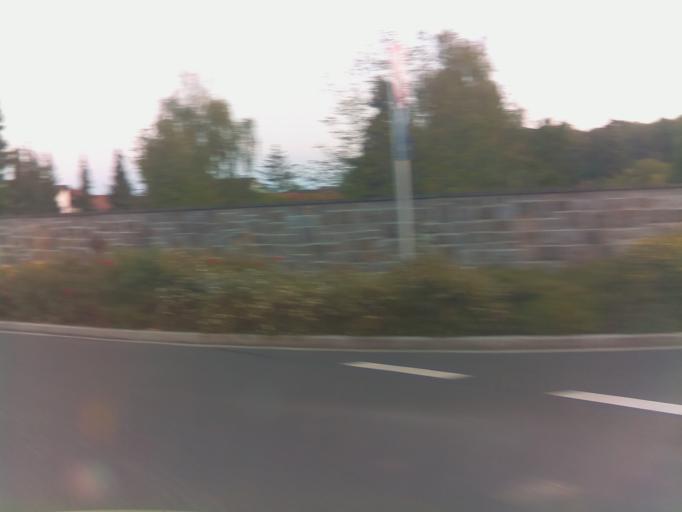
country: DE
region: Bavaria
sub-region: Regierungsbezirk Unterfranken
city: Oerlenbach
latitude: 50.1451
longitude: 10.1321
